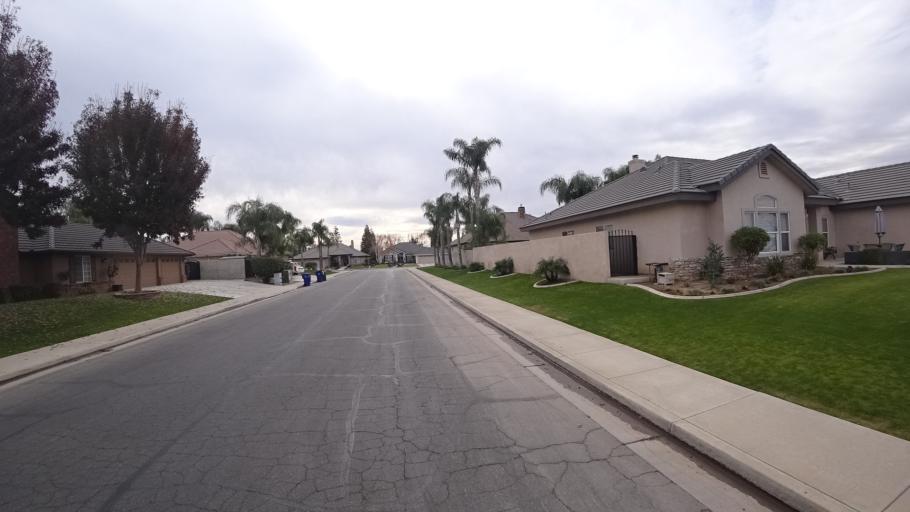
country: US
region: California
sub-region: Kern County
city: Rosedale
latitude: 35.4155
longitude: -119.1303
